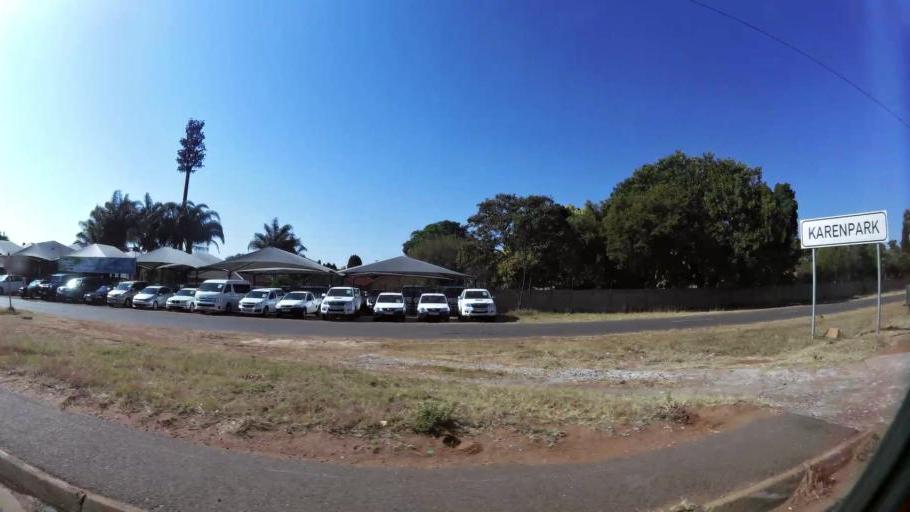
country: ZA
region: North-West
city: Ga-Rankuwa
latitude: -25.6592
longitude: 28.1018
